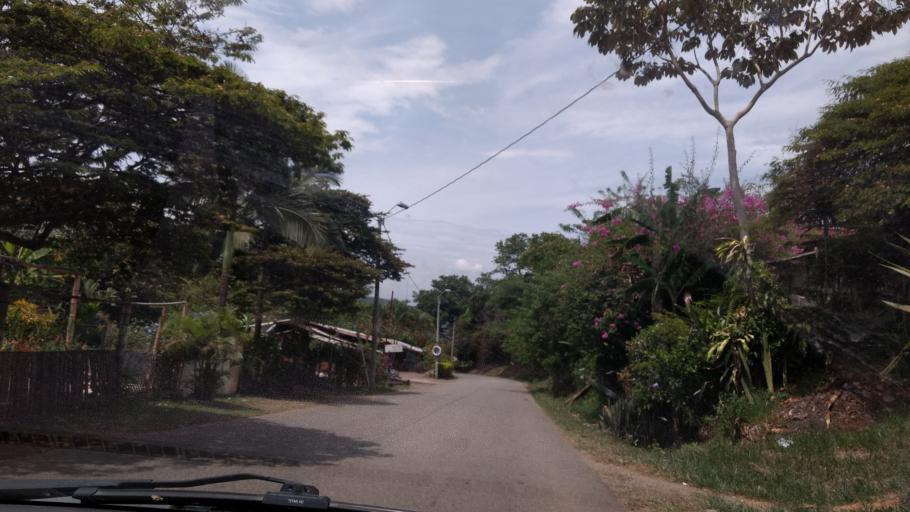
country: CO
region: Cauca
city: Buenos Aires
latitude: 3.0545
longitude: -76.6569
